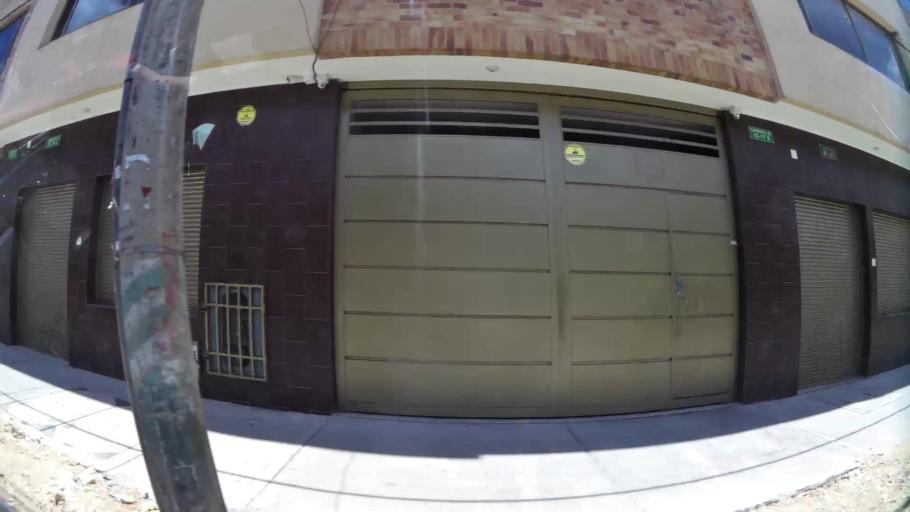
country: CO
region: Bogota D.C.
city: Bogota
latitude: 4.5921
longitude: -74.1050
